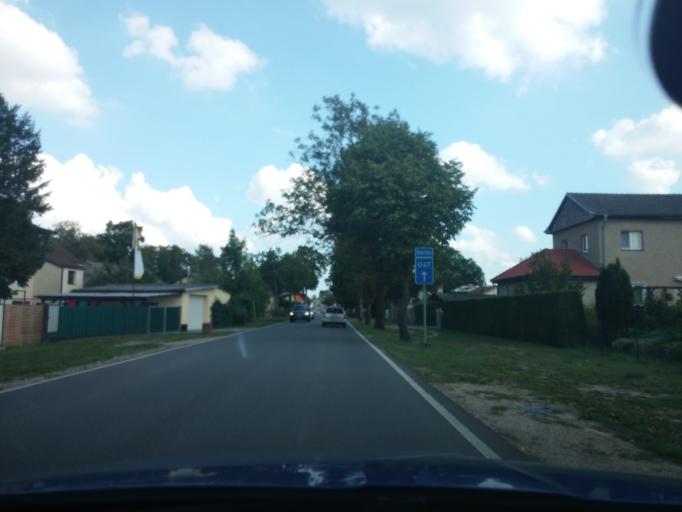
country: DE
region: Brandenburg
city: Halbe
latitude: 52.1078
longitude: 13.6927
